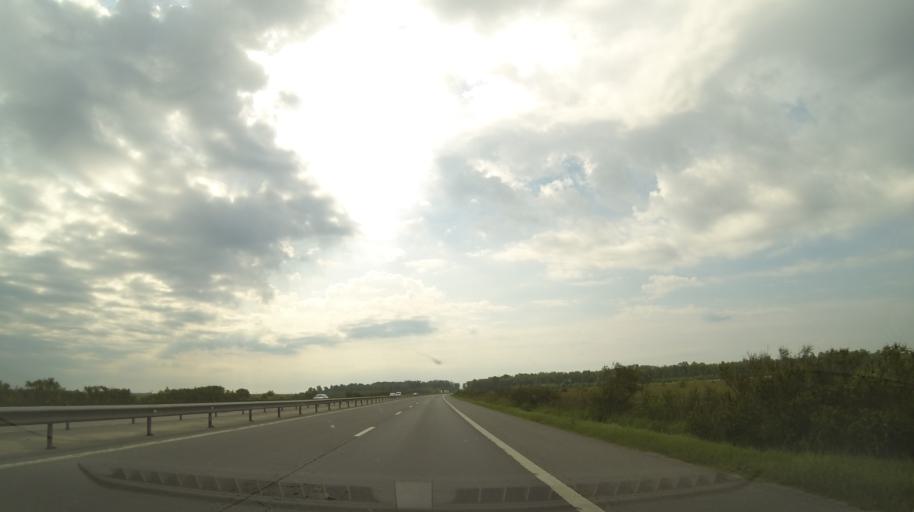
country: RO
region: Dambovita
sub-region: Comuna Uliesti
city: Uliesti
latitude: 44.6166
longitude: 25.4439
